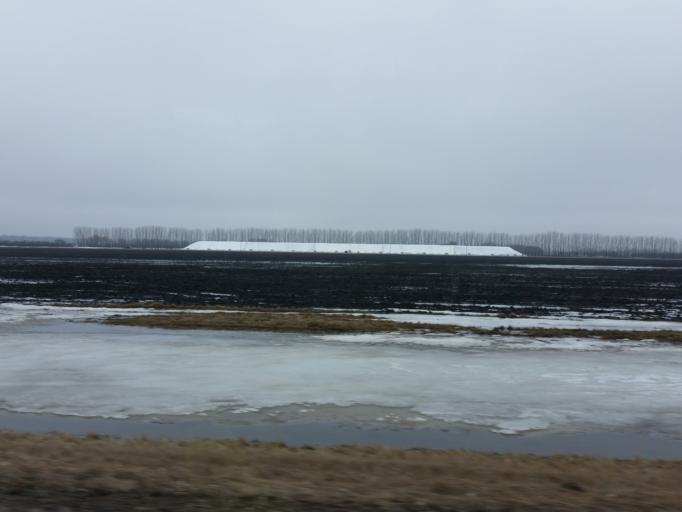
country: US
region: North Dakota
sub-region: Walsh County
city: Grafton
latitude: 48.5969
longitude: -97.4479
